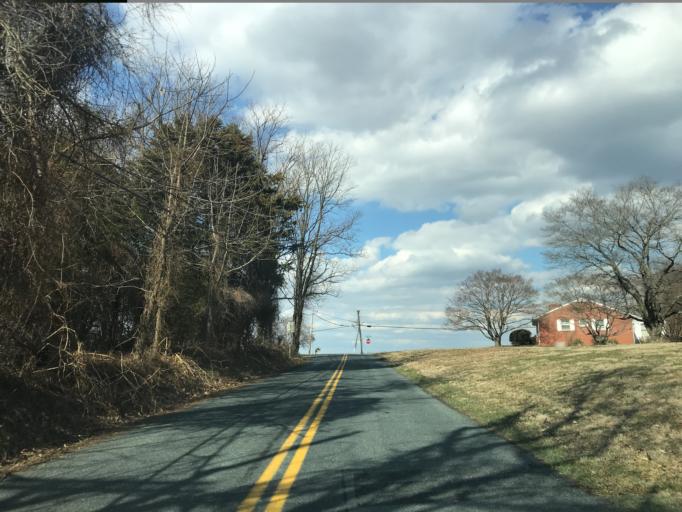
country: US
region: Maryland
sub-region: Harford County
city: Aberdeen
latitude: 39.5812
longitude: -76.1988
